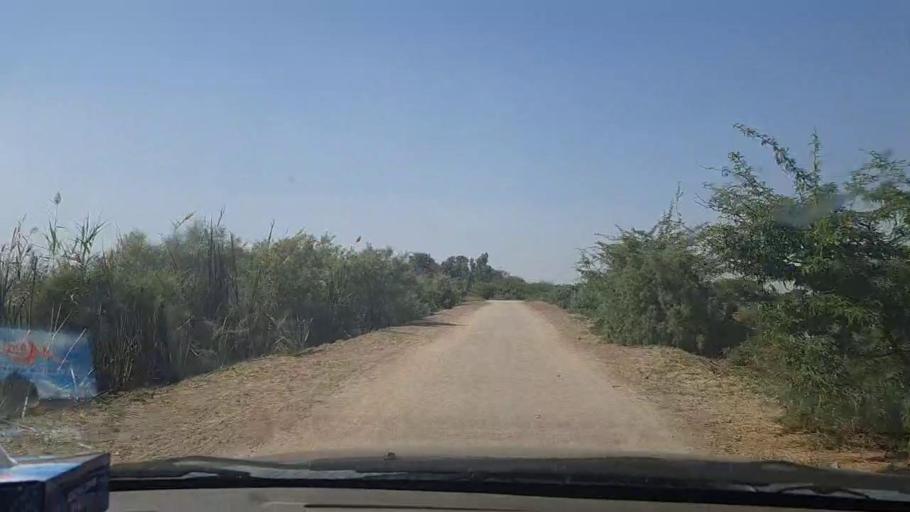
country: PK
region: Sindh
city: Chuhar Jamali
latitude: 24.2848
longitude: 67.7597
